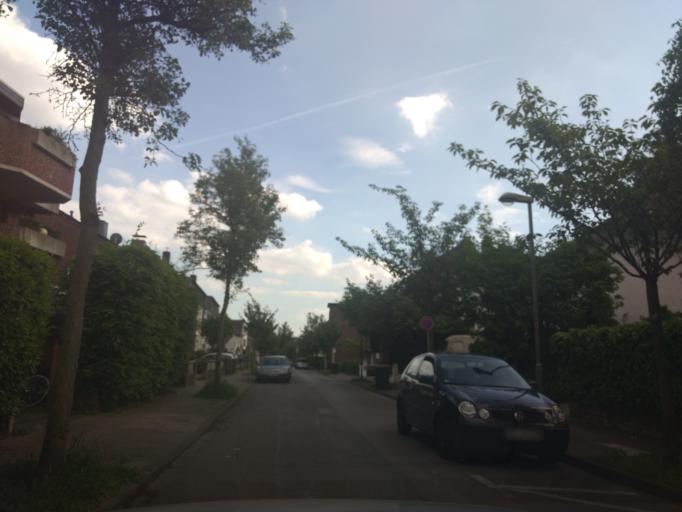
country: DE
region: North Rhine-Westphalia
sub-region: Regierungsbezirk Dusseldorf
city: Meerbusch
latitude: 51.2484
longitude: 6.7014
